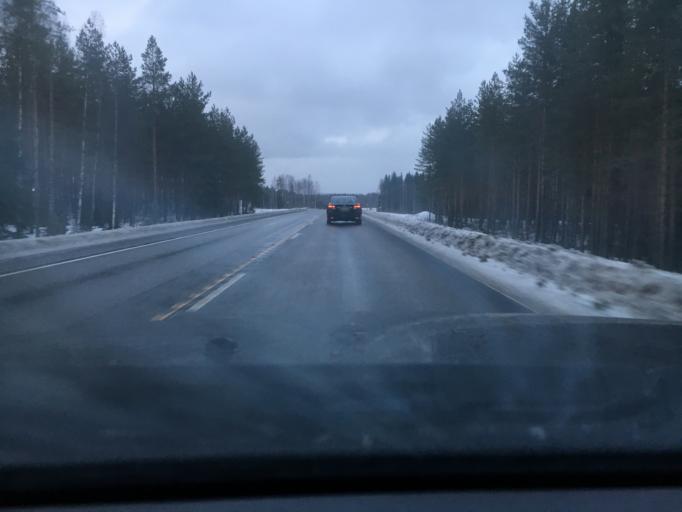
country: FI
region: Central Finland
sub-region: Jyvaeskylae
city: Hankasalmi
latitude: 62.3739
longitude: 26.5870
